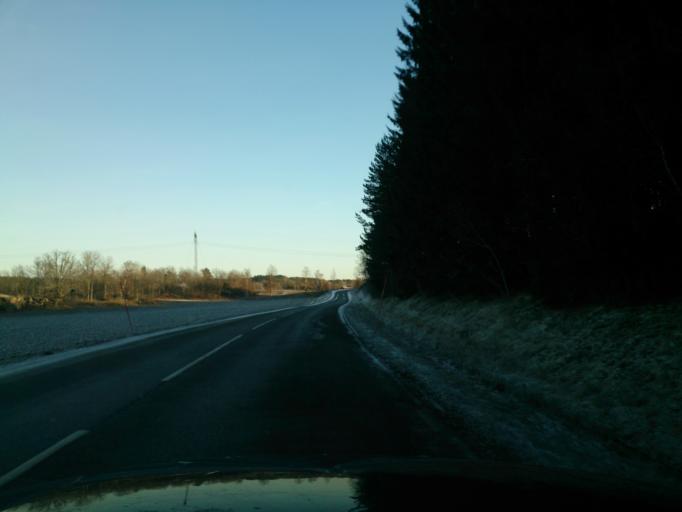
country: SE
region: OEstergoetland
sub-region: Norrkopings Kommun
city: Kimstad
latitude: 58.3840
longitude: 16.0127
